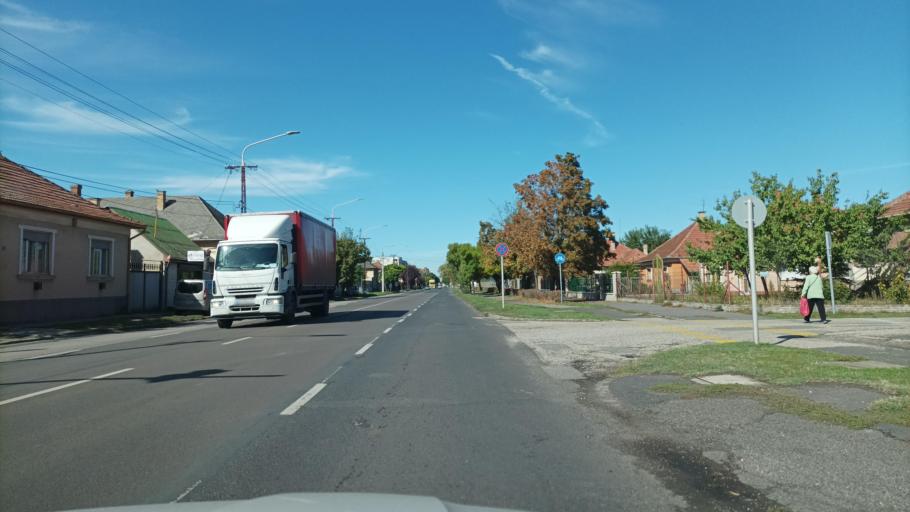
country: HU
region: Pest
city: Cegled
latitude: 47.1745
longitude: 19.8074
